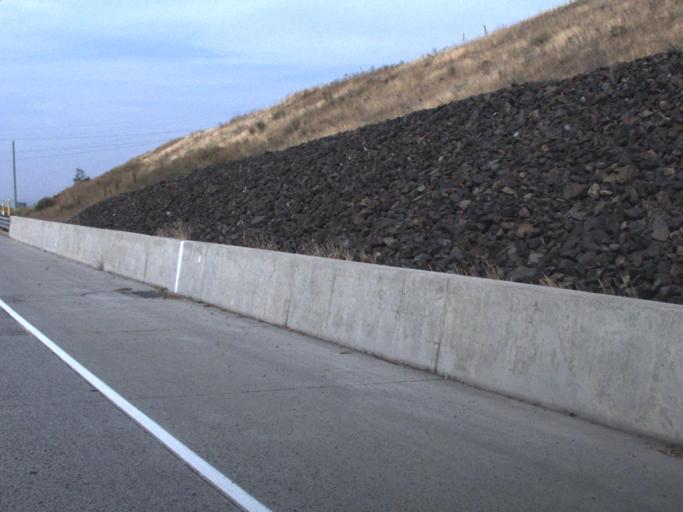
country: US
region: Washington
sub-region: Spokane County
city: Mead
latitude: 47.7396
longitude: -117.3607
